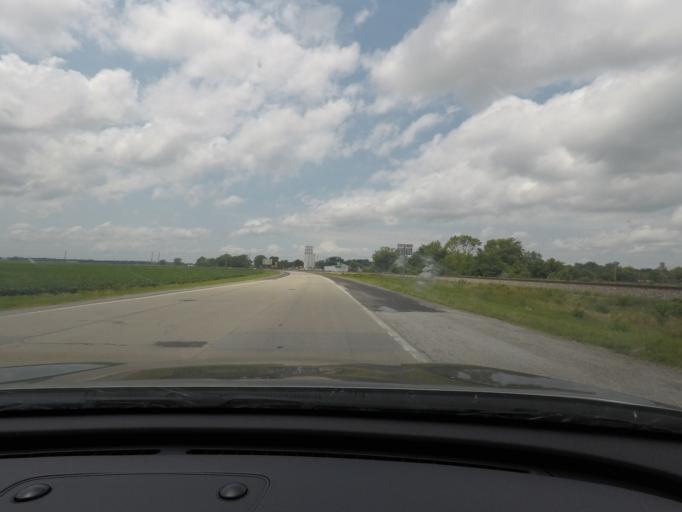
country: US
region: Missouri
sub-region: Carroll County
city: Carrollton
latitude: 39.3393
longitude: -93.4922
